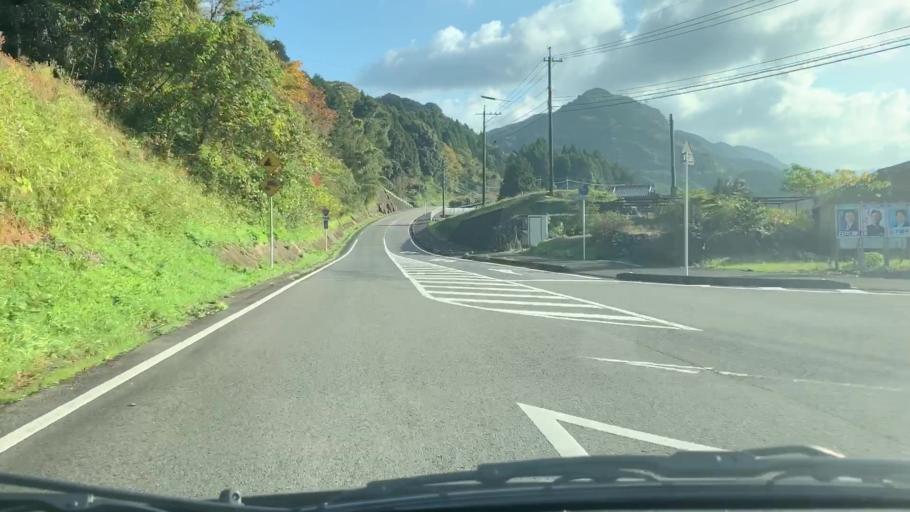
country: JP
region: Saga Prefecture
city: Kashima
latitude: 33.0570
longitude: 130.0707
